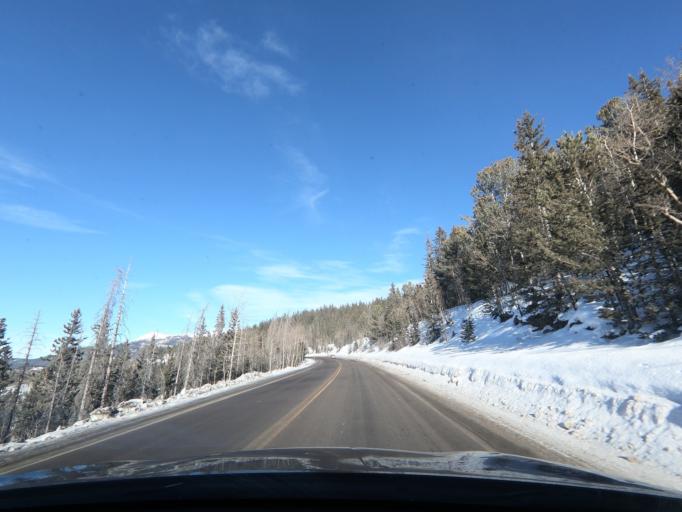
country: US
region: Colorado
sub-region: Teller County
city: Cripple Creek
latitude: 38.7634
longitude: -105.1553
